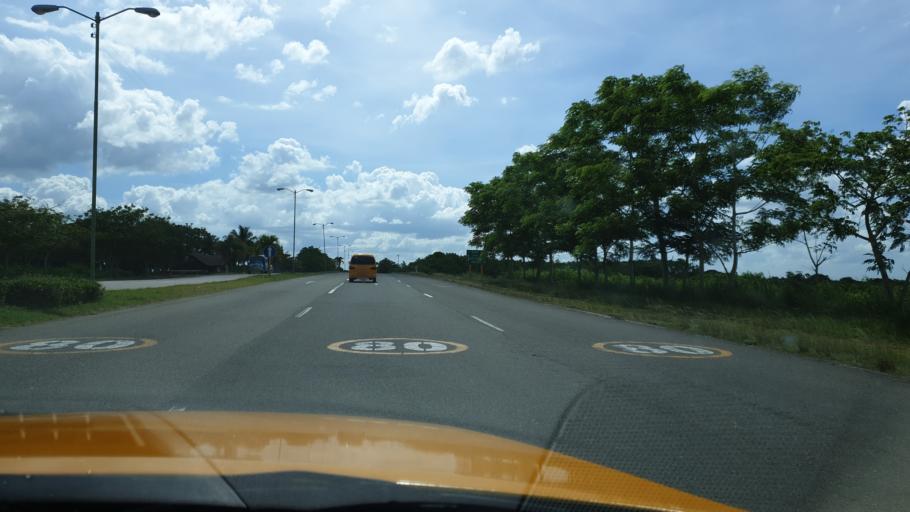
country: CU
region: Cienfuegos
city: Cruces
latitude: 22.4529
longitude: -80.2898
